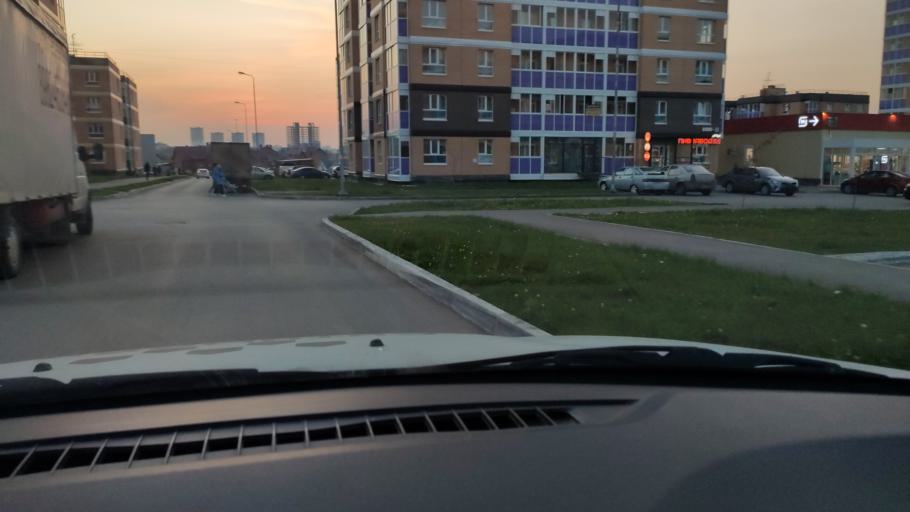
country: RU
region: Perm
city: Perm
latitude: 58.0043
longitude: 56.3373
